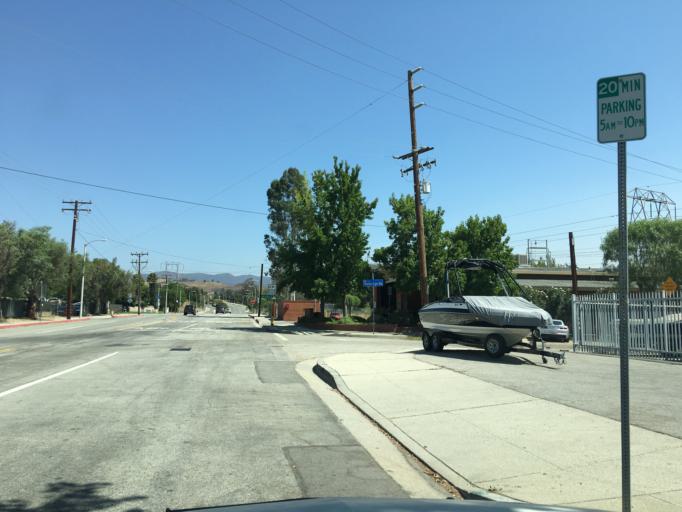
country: US
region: California
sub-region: Los Angeles County
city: Castaic
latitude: 34.4961
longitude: -118.6164
